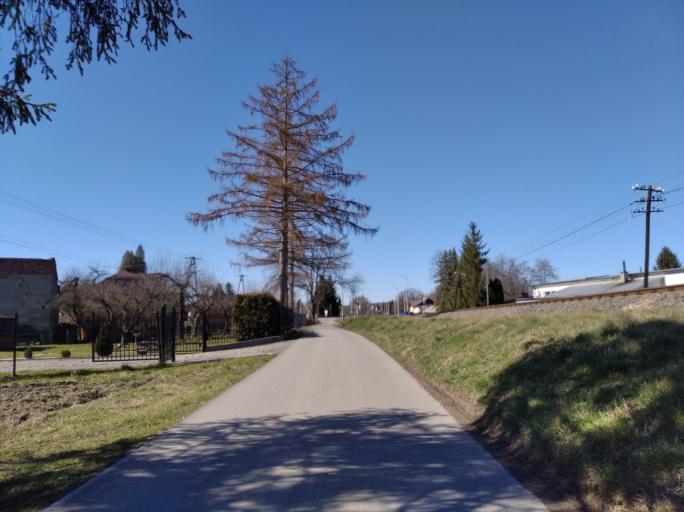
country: PL
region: Subcarpathian Voivodeship
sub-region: Powiat strzyzowski
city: Wysoka Strzyzowska
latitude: 49.8719
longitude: 21.7473
